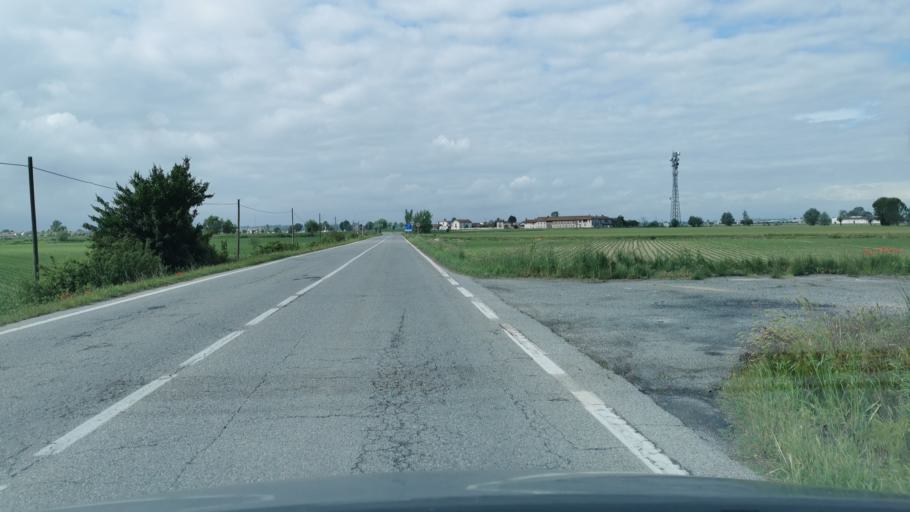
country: IT
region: Piedmont
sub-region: Provincia di Torino
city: Carmagnola
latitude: 44.8203
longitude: 7.7076
